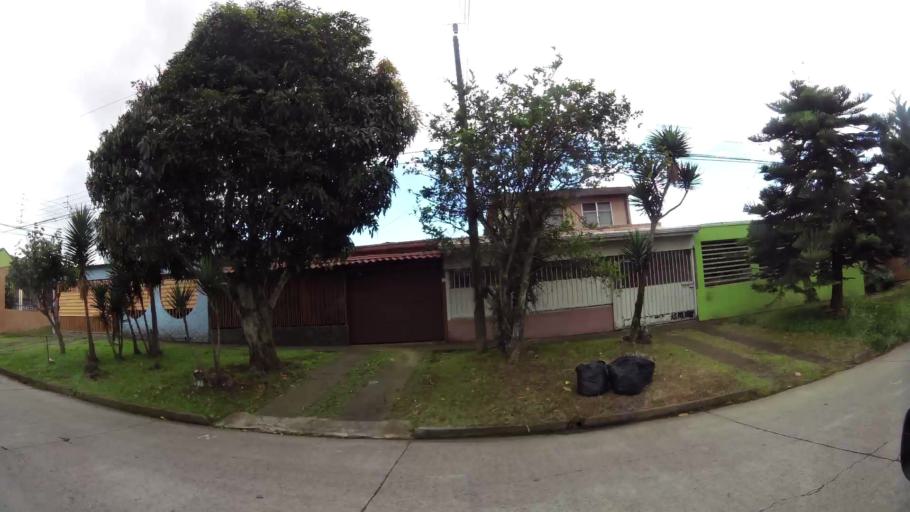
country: CR
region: San Jose
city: Curridabat
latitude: 9.9204
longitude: -84.0394
